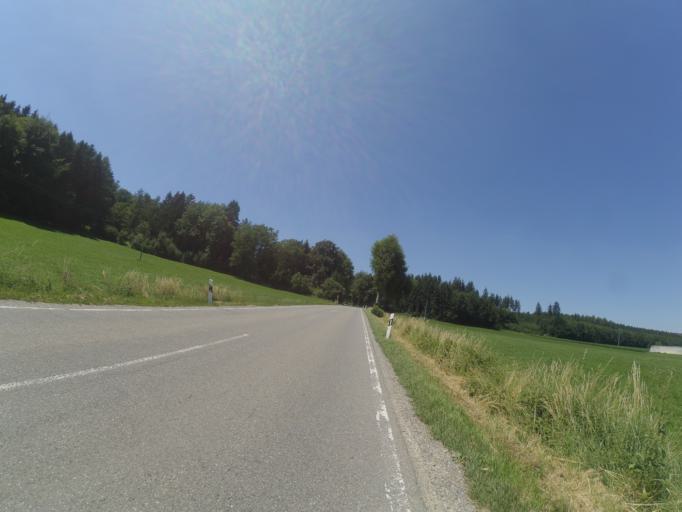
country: DE
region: Baden-Wuerttemberg
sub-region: Tuebingen Region
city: Bad Waldsee
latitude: 47.9002
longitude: 9.7866
